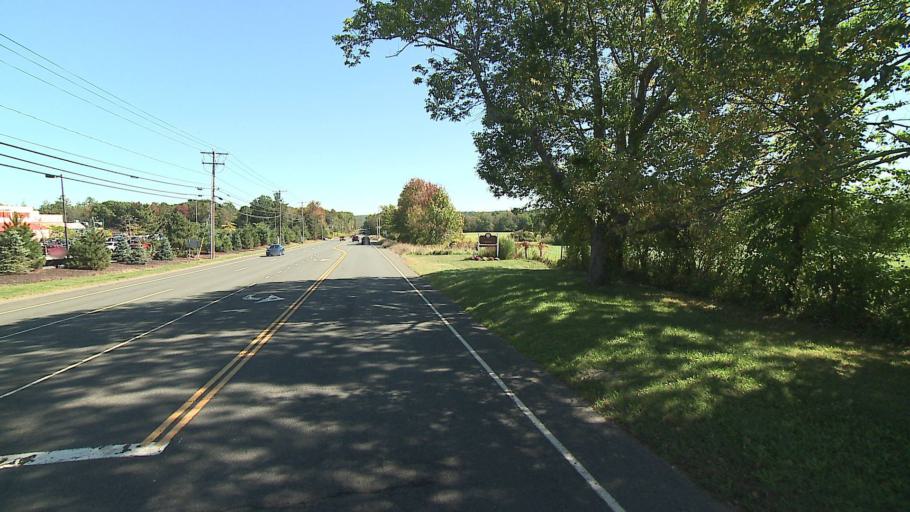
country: US
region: Connecticut
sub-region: Litchfield County
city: Northwest Harwinton
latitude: 41.8211
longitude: -73.0700
